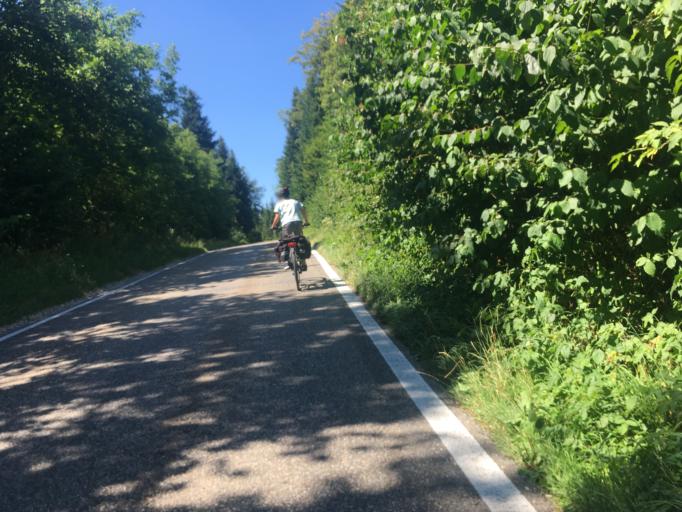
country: CH
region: Bern
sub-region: Seeland District
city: Grossaffoltern
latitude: 47.0916
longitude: 7.3724
